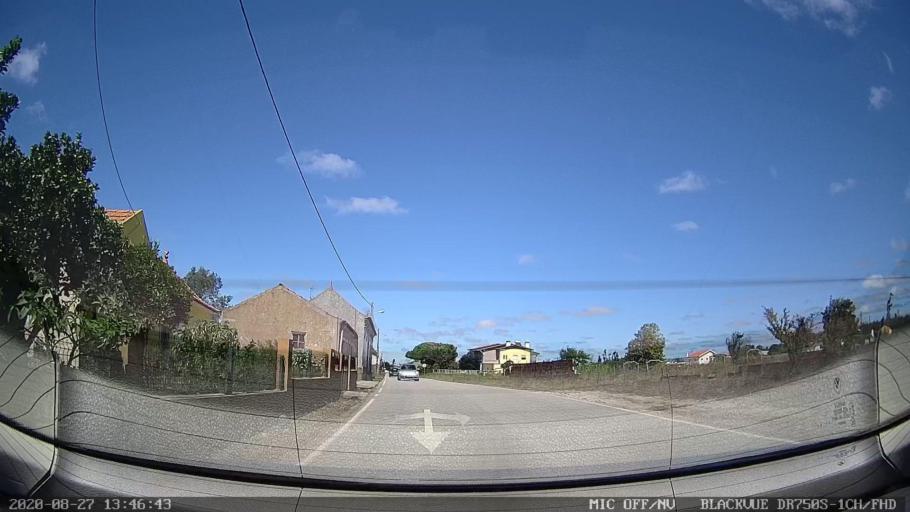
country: PT
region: Coimbra
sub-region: Mira
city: Mira
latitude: 40.3938
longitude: -8.7359
